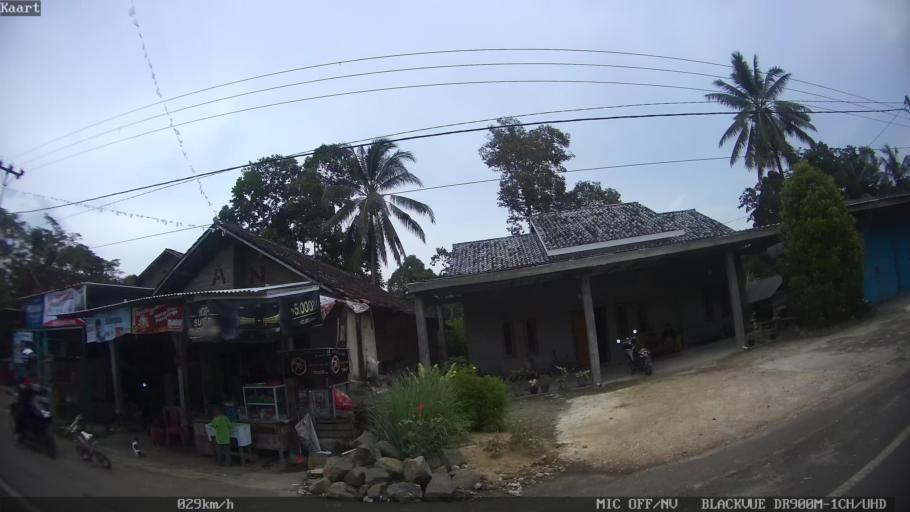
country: ID
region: Lampung
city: Bandarlampung
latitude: -5.4364
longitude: 105.2212
